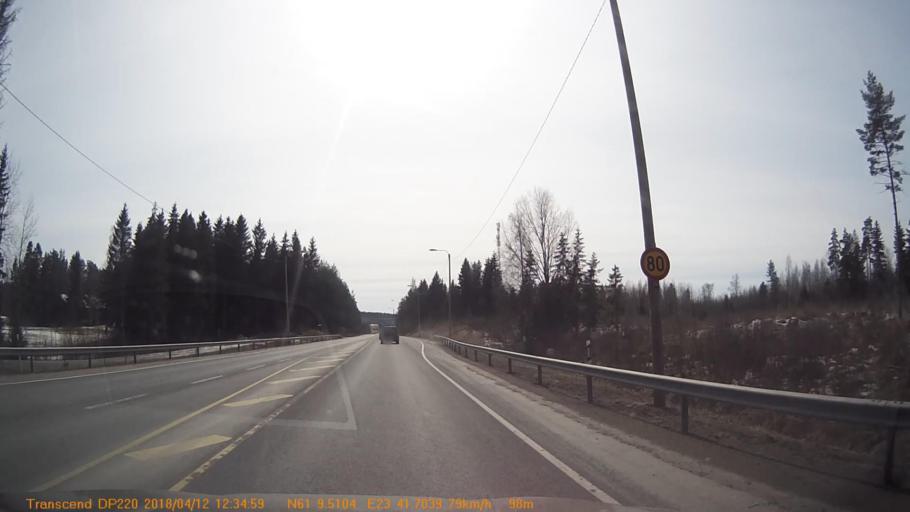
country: FI
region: Pirkanmaa
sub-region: Etelae-Pirkanmaa
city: Kylmaekoski
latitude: 61.1586
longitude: 23.6951
